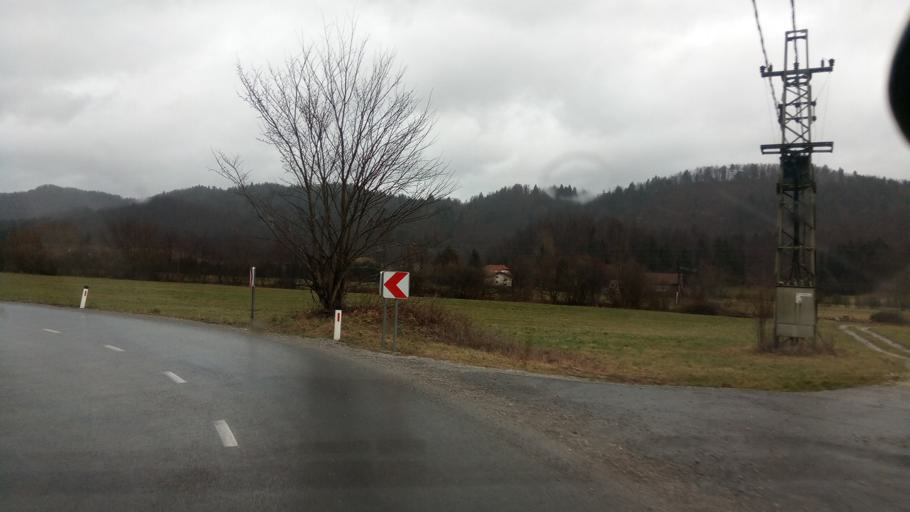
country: SI
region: Vrhnika
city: Vrhnika
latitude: 45.9883
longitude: 14.2686
